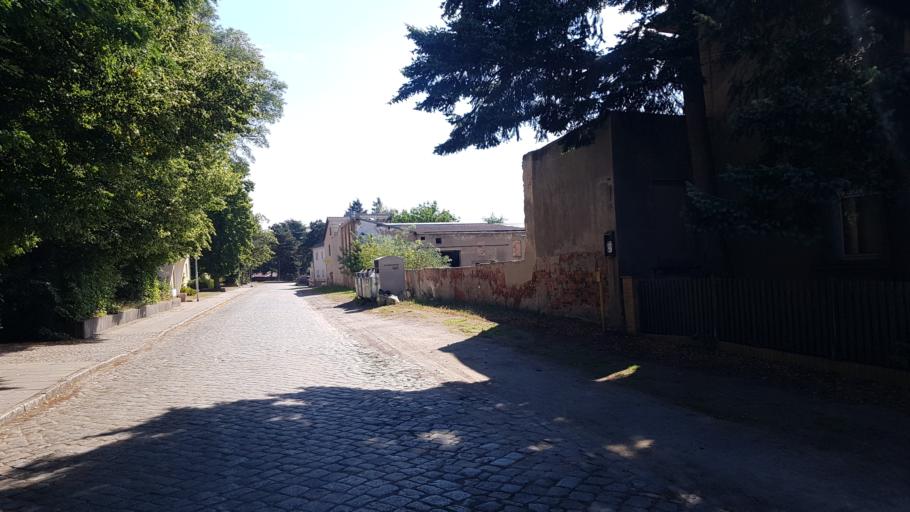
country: DE
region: Brandenburg
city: Plessa
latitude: 51.4700
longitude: 13.6172
